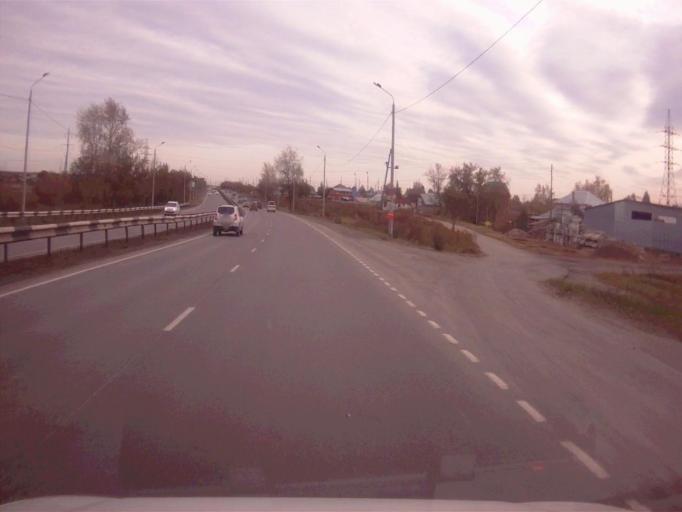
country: RU
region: Chelyabinsk
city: Novosineglazovskiy
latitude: 55.0472
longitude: 61.4166
